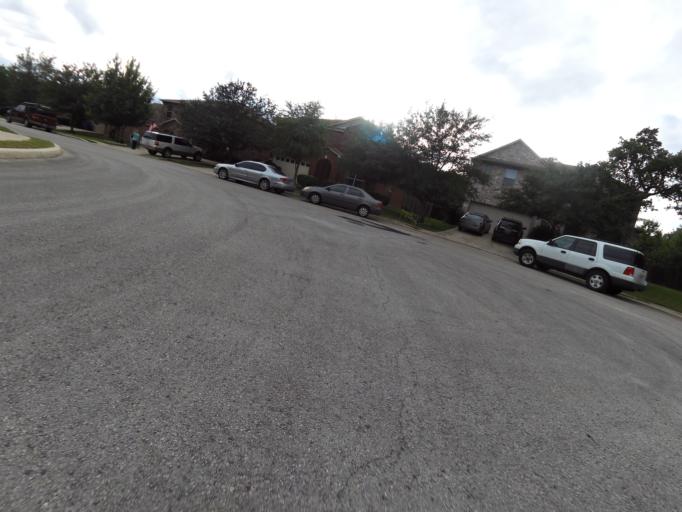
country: US
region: Texas
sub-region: Bexar County
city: Cross Mountain
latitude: 29.6723
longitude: -98.6401
